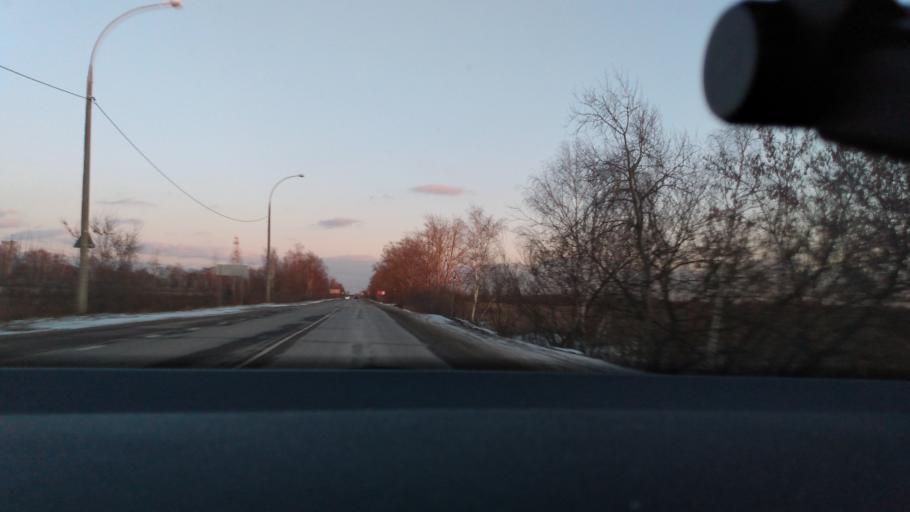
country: RU
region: Moskovskaya
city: Kolomna
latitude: 55.0891
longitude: 38.9100
